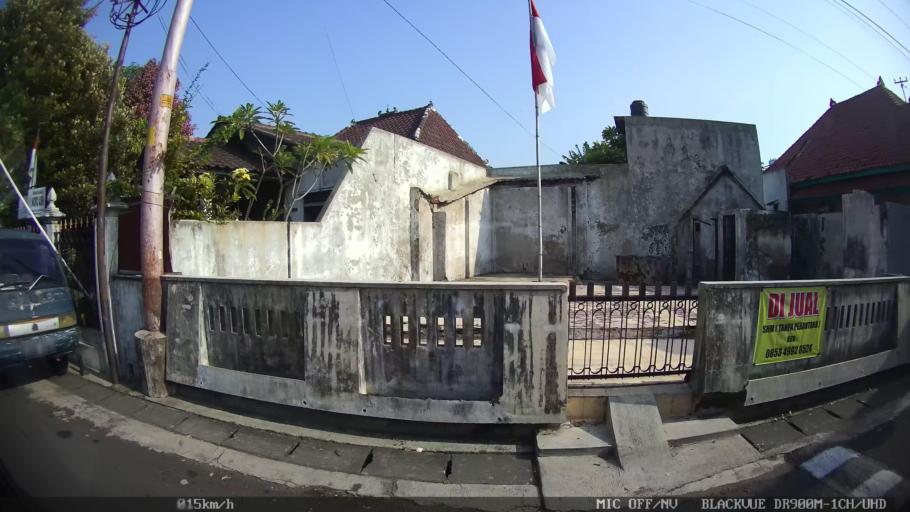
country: ID
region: Daerah Istimewa Yogyakarta
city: Yogyakarta
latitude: -7.8066
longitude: 110.3654
